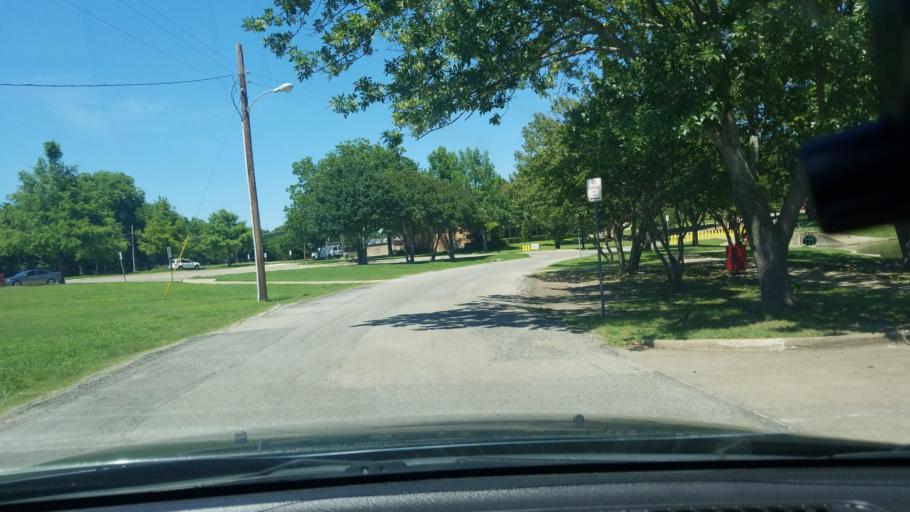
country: US
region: Texas
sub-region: Dallas County
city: Mesquite
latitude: 32.7632
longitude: -96.6006
